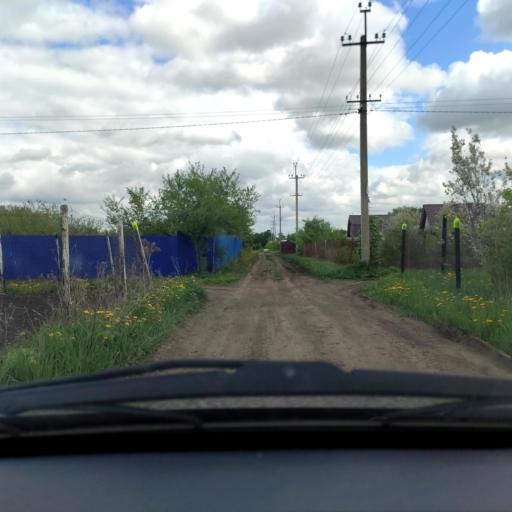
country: RU
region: Bashkortostan
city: Kabakovo
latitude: 54.7092
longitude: 56.1582
